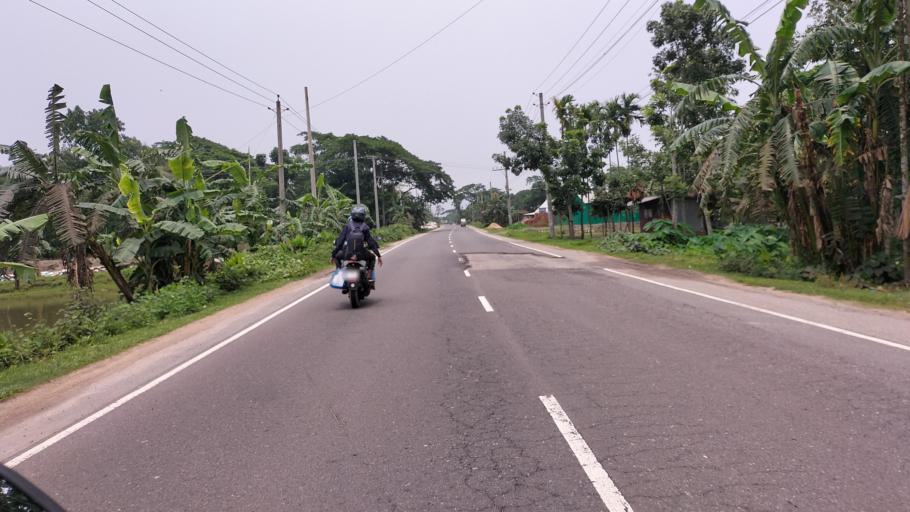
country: BD
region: Dhaka
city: Mymensingh
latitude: 24.7770
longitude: 90.4692
